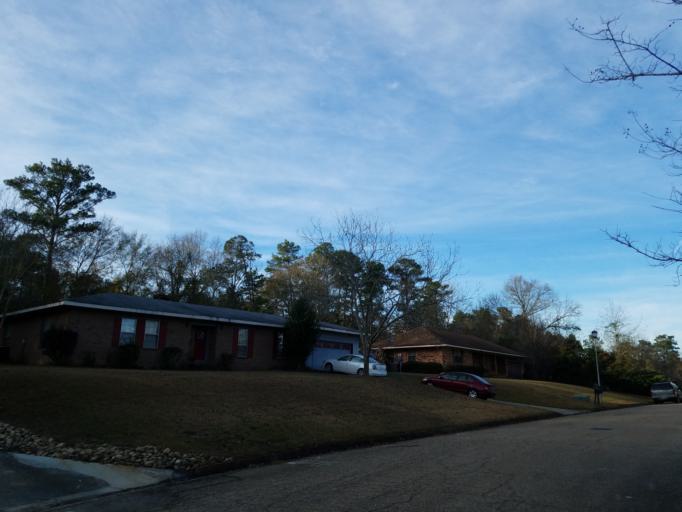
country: US
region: Mississippi
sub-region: Lamar County
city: West Hattiesburg
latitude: 31.3114
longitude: -89.3514
